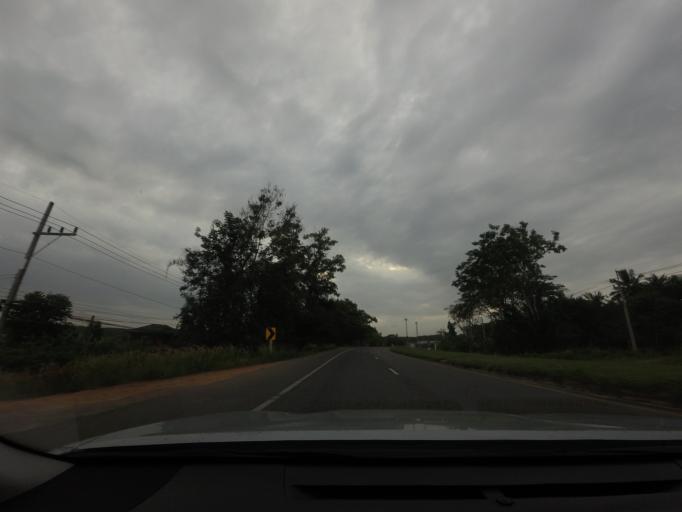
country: TH
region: Surat Thani
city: Phunphin
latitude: 9.0365
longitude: 99.1380
